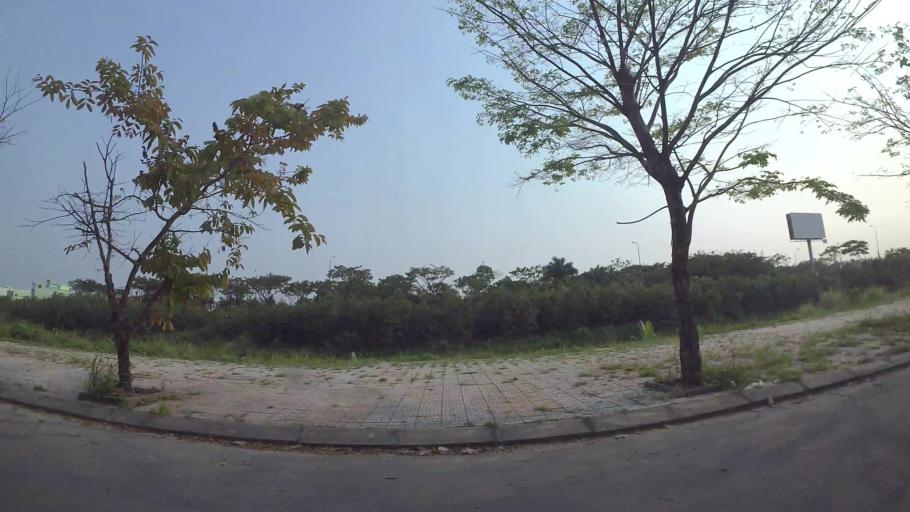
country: VN
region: Da Nang
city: Cam Le
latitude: 16.0158
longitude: 108.1943
